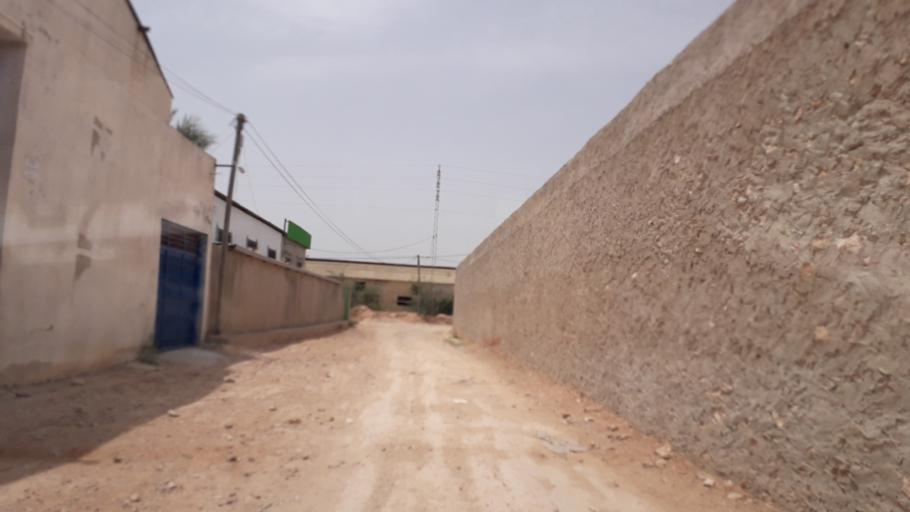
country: TN
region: Safaqis
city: Al Qarmadah
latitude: 34.8504
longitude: 10.7644
